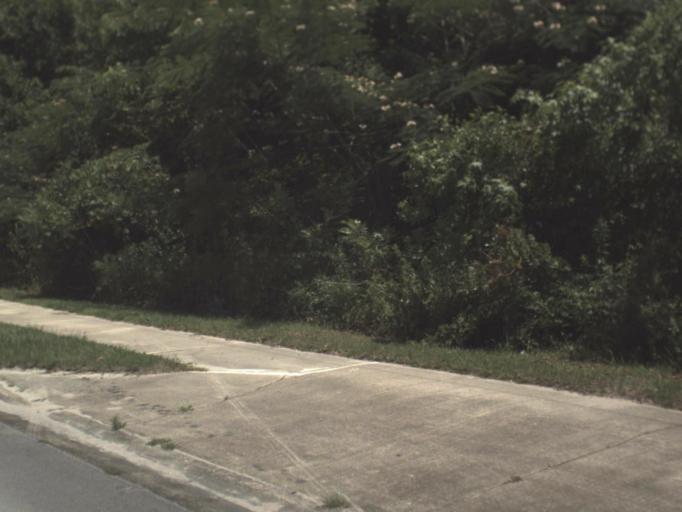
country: US
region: Florida
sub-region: Alachua County
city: Alachua
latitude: 29.6599
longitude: -82.4710
